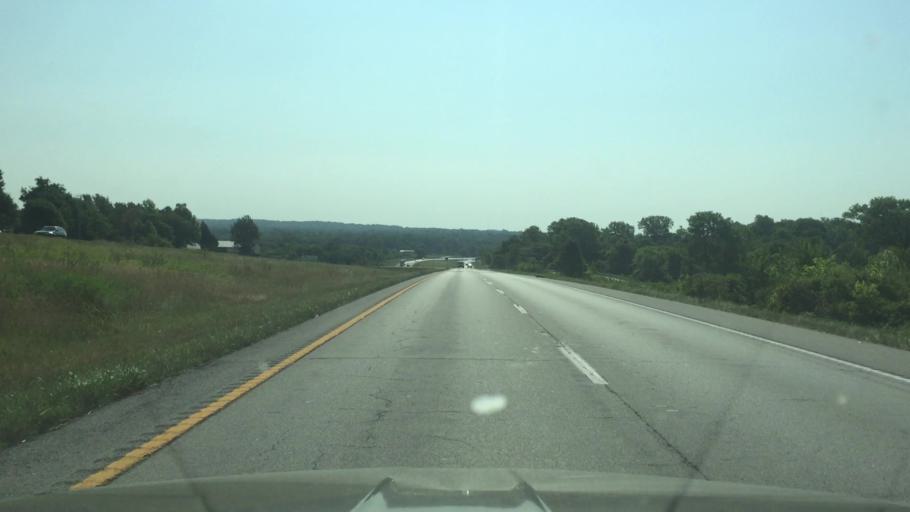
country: US
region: Missouri
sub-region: Jackson County
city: Lone Jack
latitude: 38.8731
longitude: -94.1473
